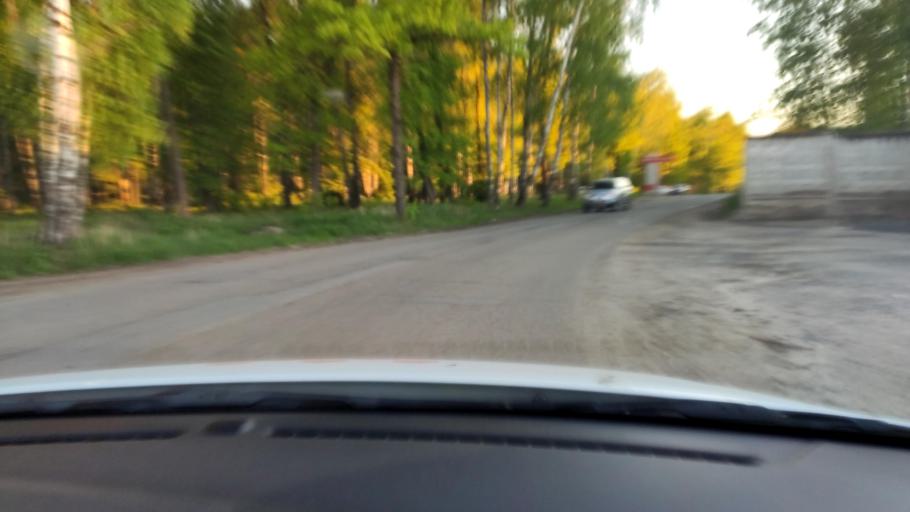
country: RU
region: Tatarstan
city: Vysokaya Gora
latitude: 55.9279
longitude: 49.3110
